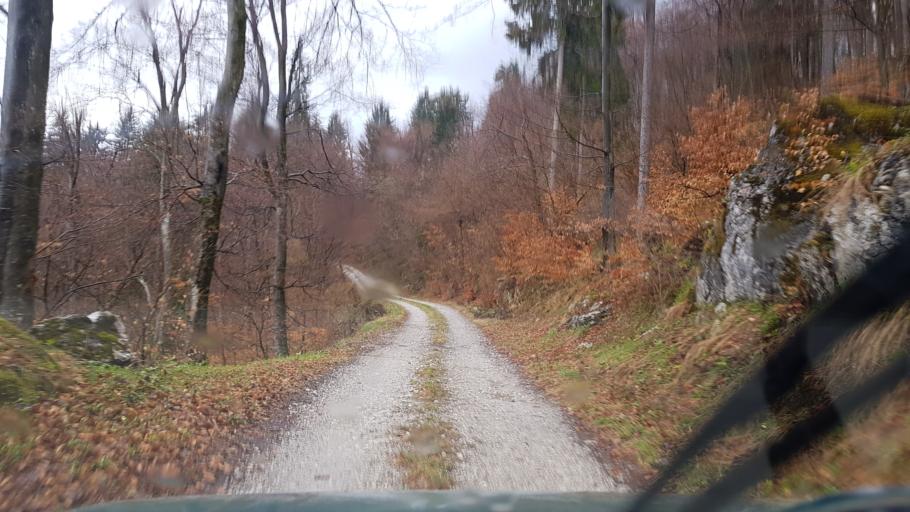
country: SI
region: Cerkno
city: Cerkno
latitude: 46.1318
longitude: 13.8675
